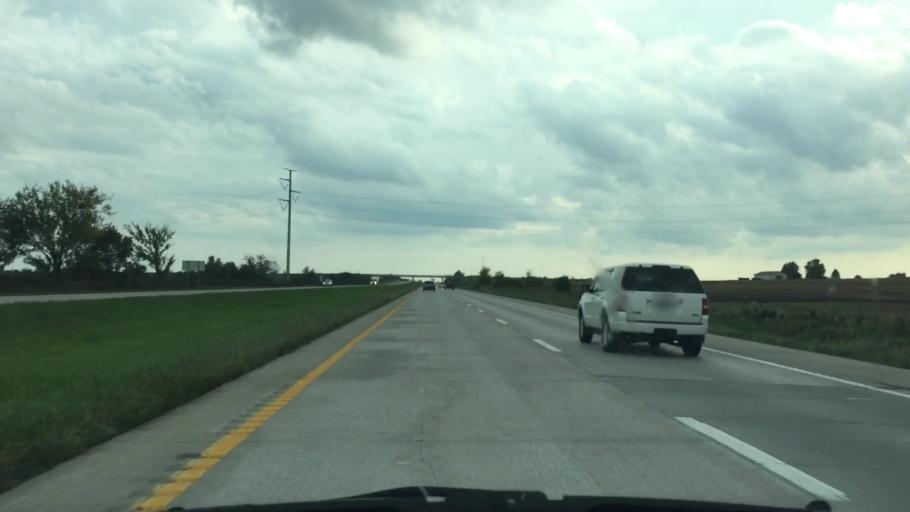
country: US
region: Missouri
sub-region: Clinton County
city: Cameron
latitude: 39.6385
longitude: -94.2432
